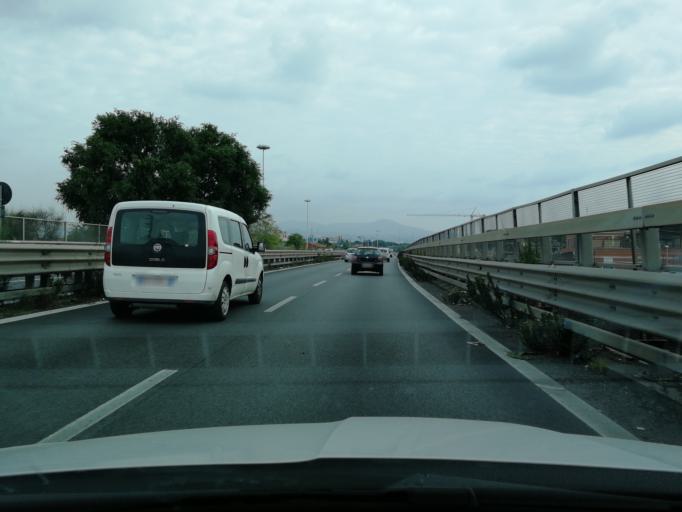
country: IT
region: Latium
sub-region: Citta metropolitana di Roma Capitale
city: Ciampino
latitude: 41.8427
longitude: 12.5842
